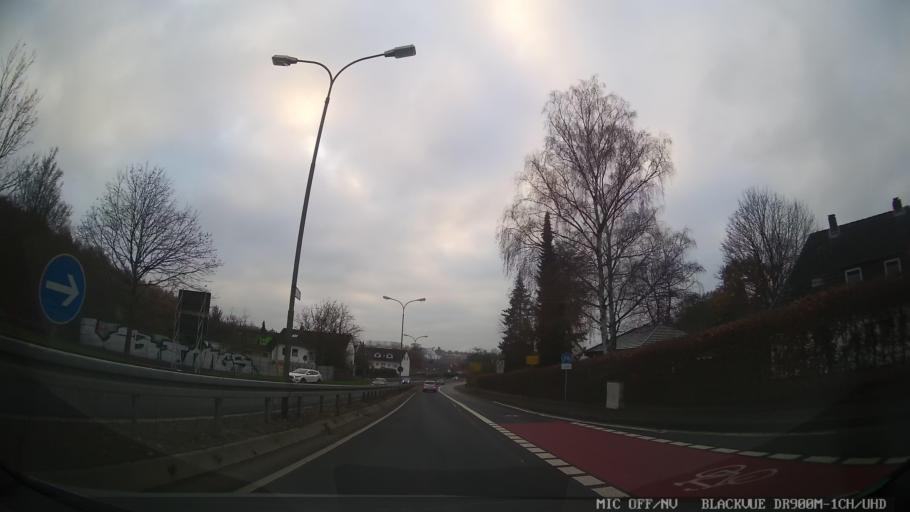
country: DE
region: Hesse
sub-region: Regierungsbezirk Giessen
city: Marburg an der Lahn
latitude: 50.8013
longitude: 8.7935
